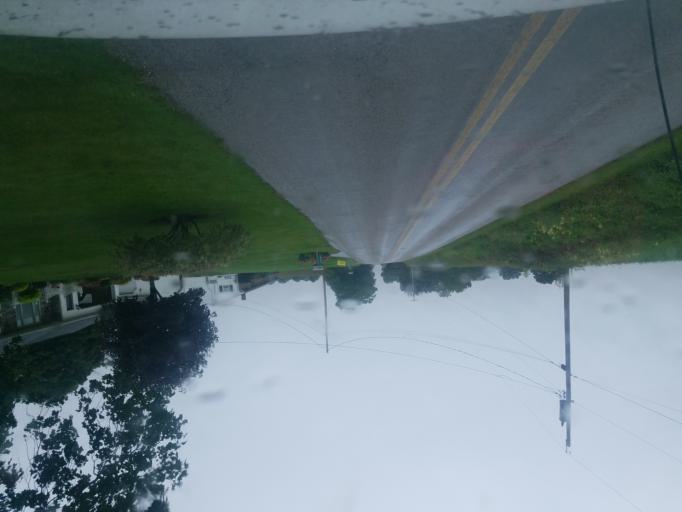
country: US
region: Ohio
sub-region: Wayne County
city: Rittman
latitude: 40.9780
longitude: -81.8114
